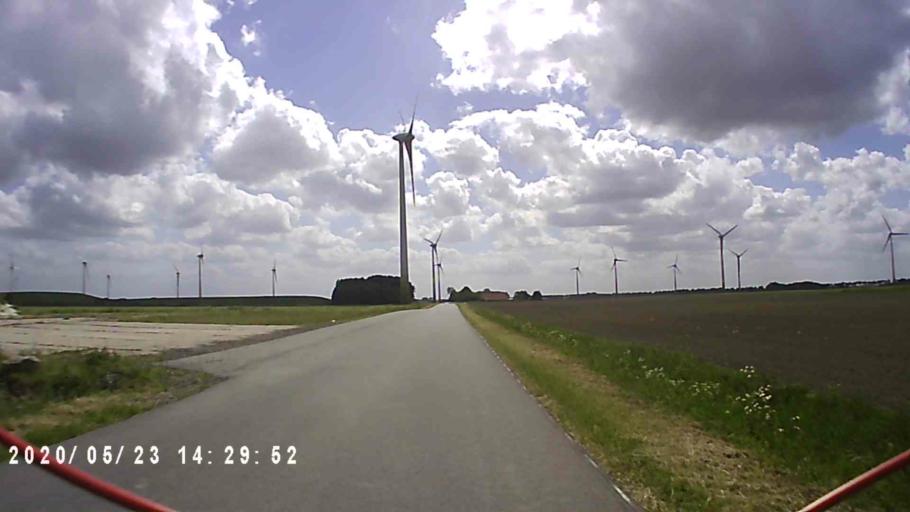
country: NL
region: Groningen
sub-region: Gemeente Delfzijl
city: Delfzijl
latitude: 53.2901
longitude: 6.9676
